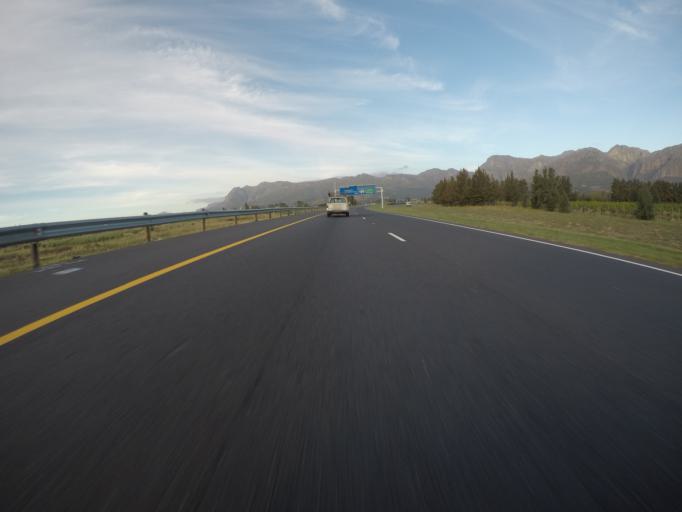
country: ZA
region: Western Cape
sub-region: Cape Winelands District Municipality
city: Paarl
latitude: -33.7428
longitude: 19.0037
